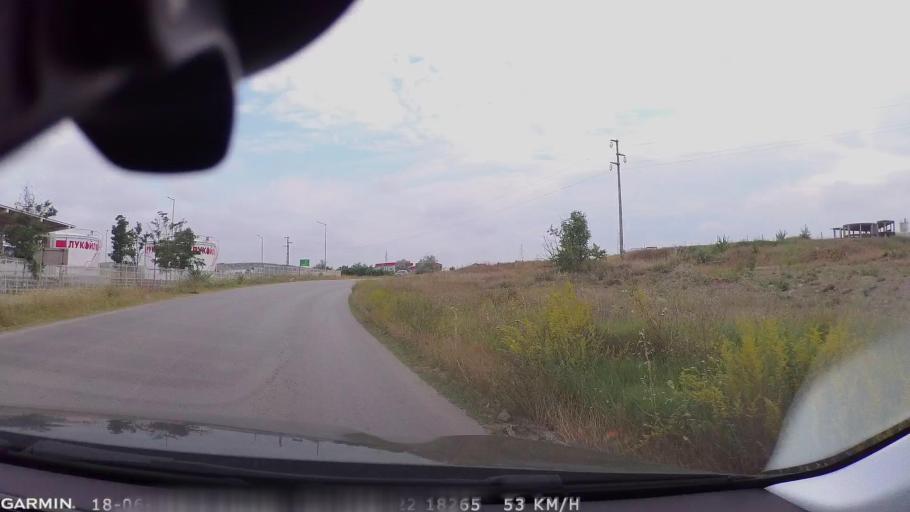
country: MK
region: Stip
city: Shtip
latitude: 41.7726
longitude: 22.1826
